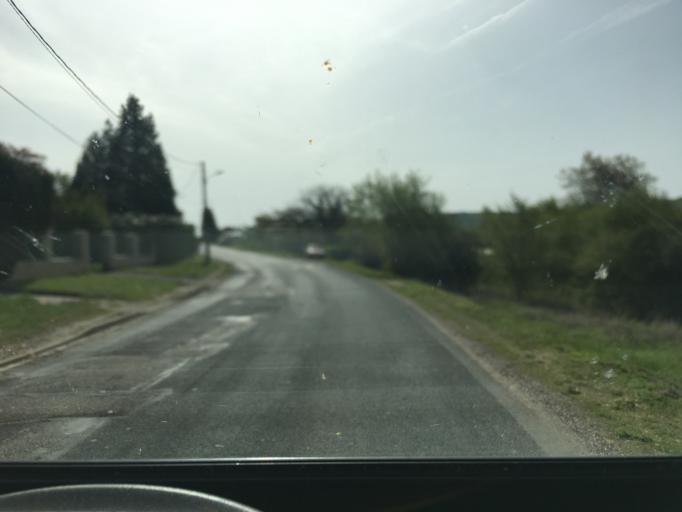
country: FR
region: Lorraine
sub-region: Departement de Meurthe-et-Moselle
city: Chaligny
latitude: 48.6305
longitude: 6.0501
